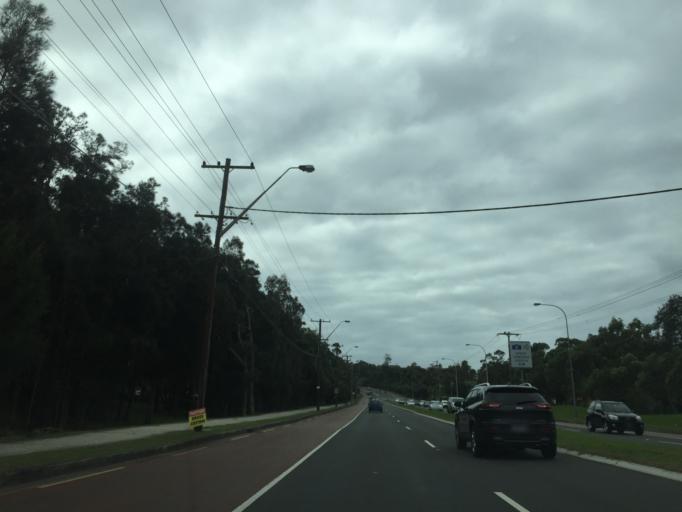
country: AU
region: New South Wales
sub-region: Pittwater
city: Warriewood
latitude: -33.6951
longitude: 151.3024
